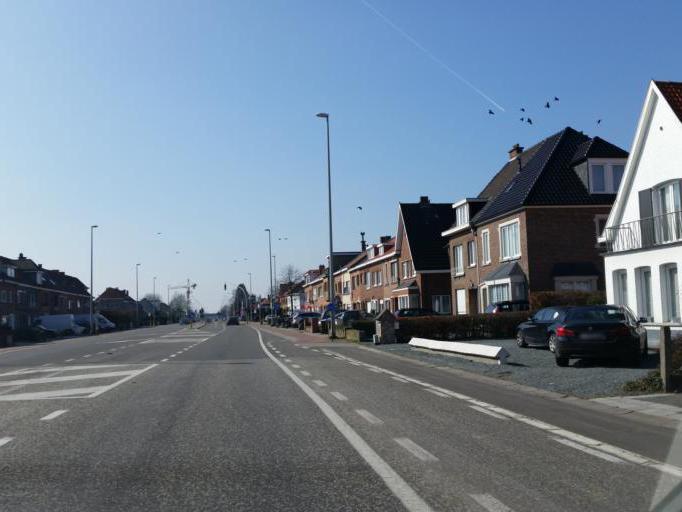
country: BE
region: Flanders
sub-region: Provincie Oost-Vlaanderen
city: Sint-Niklaas
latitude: 51.1512
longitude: 4.1352
